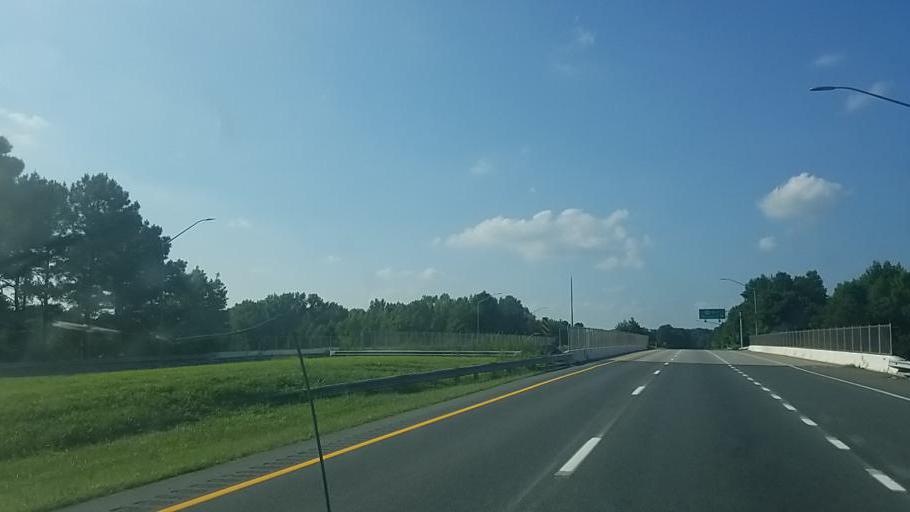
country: US
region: Maryland
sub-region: Worcester County
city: Berlin
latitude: 38.3419
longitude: -75.2132
